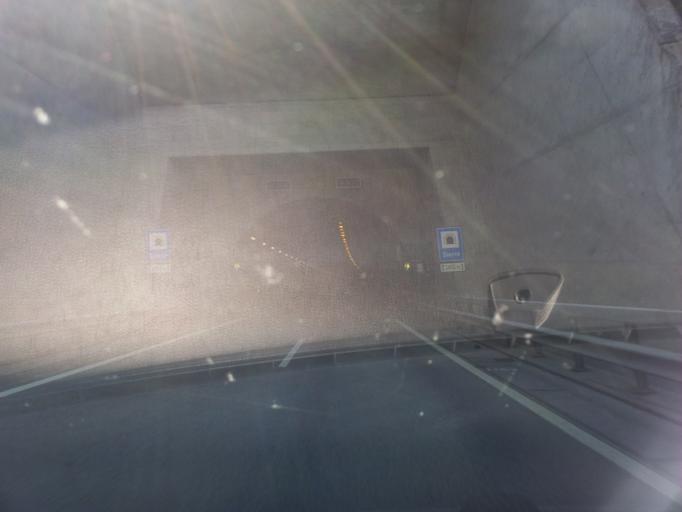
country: CH
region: Valais
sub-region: Sierre District
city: Chippis
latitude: 46.2854
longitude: 7.5477
